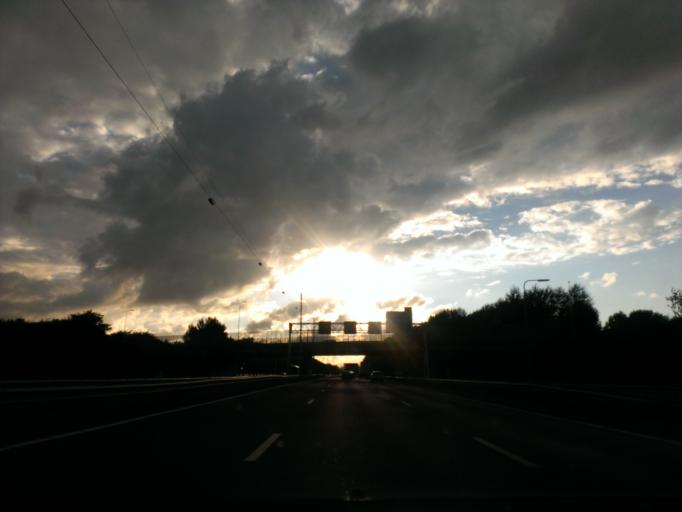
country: NL
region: South Holland
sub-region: Gemeente Hendrik-Ido-Ambacht
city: Hendrik-Ido-Ambacht
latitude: 51.8565
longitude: 4.6271
